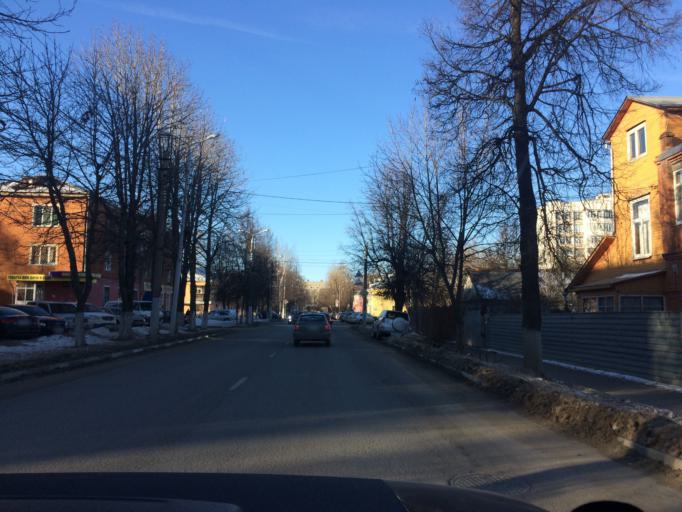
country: RU
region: Tula
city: Mendeleyevskiy
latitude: 54.1706
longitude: 37.5787
